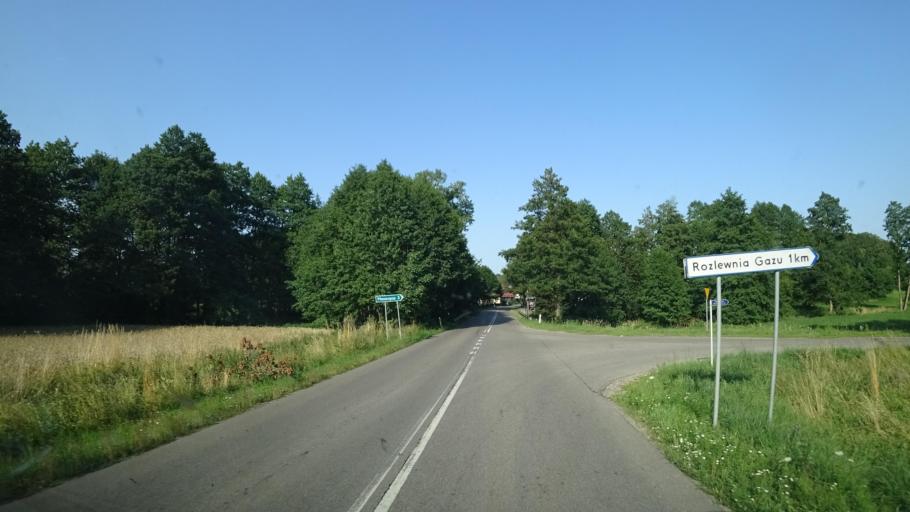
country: PL
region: Pomeranian Voivodeship
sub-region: Powiat czluchowski
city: Przechlewo
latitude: 53.8061
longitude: 17.3304
